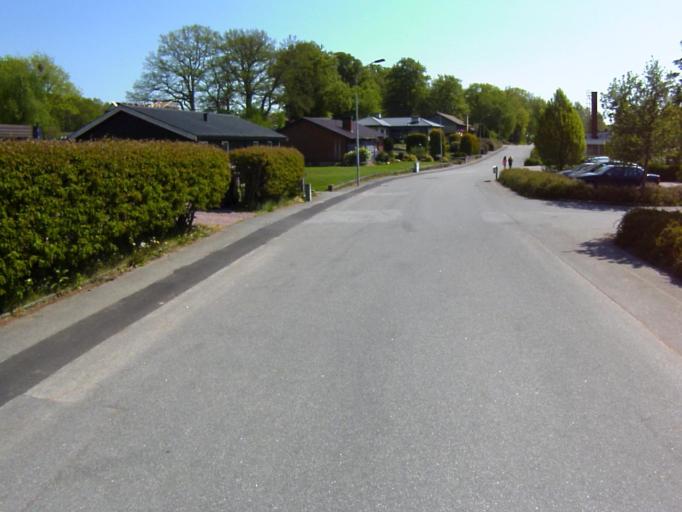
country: SE
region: Skane
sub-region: Kristianstads Kommun
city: Tollarp
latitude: 56.1736
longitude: 14.2865
